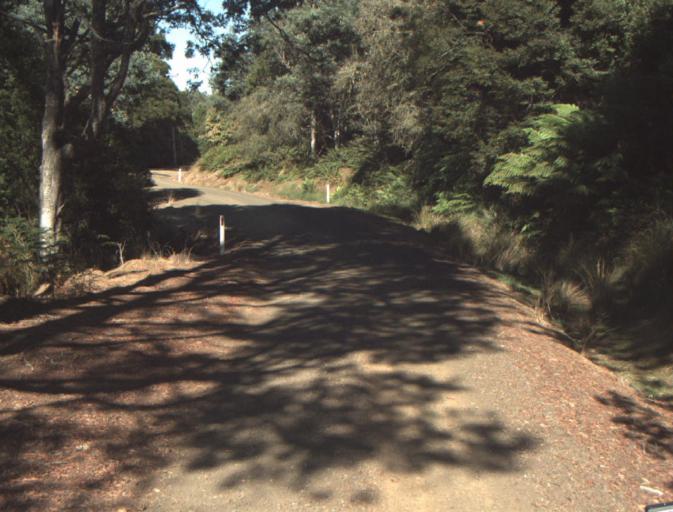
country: AU
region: Tasmania
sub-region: Dorset
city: Scottsdale
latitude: -41.2912
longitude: 147.3571
